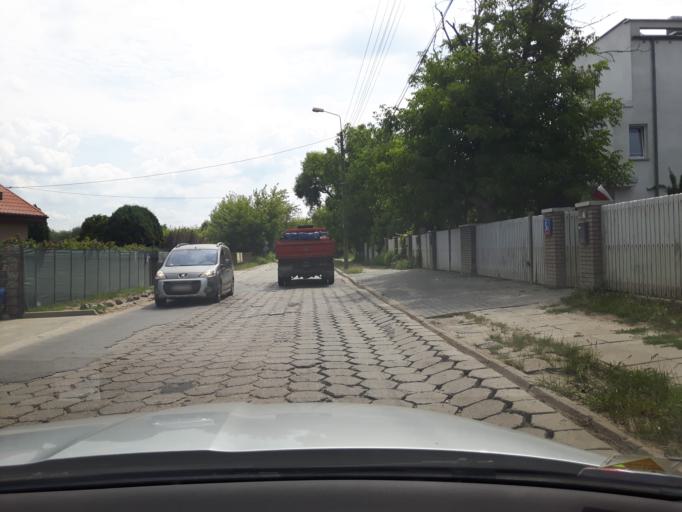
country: PL
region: Masovian Voivodeship
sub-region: Warszawa
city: Wilanow
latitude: 52.2002
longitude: 21.0781
